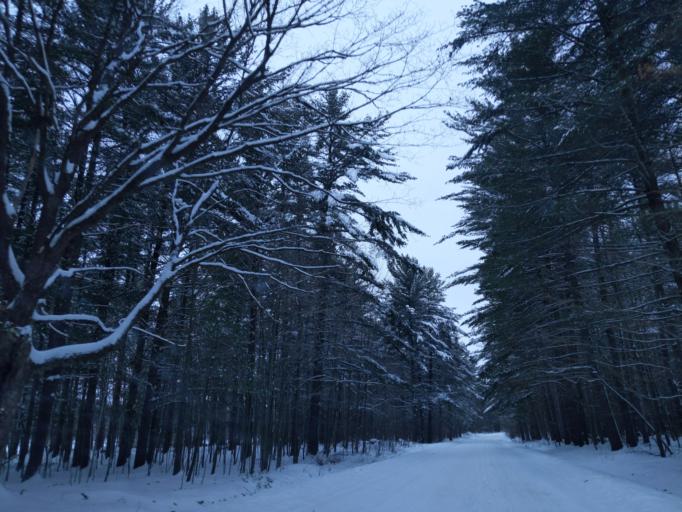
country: US
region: Wisconsin
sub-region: Marathon County
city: Marathon
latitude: 44.7681
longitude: -89.8695
